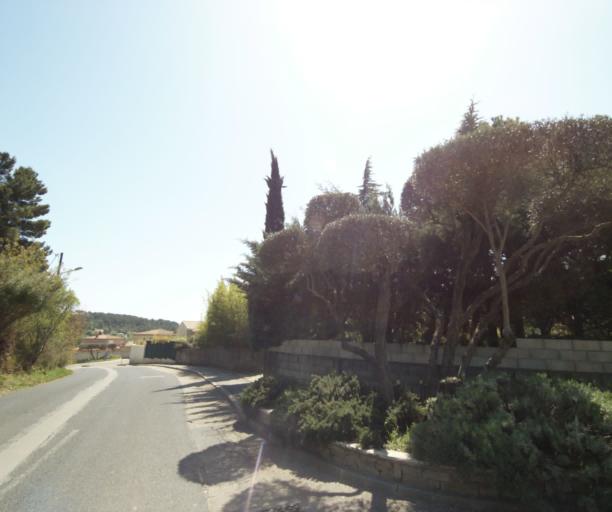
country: FR
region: Languedoc-Roussillon
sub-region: Departement de l'Herault
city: Prades-le-Lez
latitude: 43.6952
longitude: 3.8704
